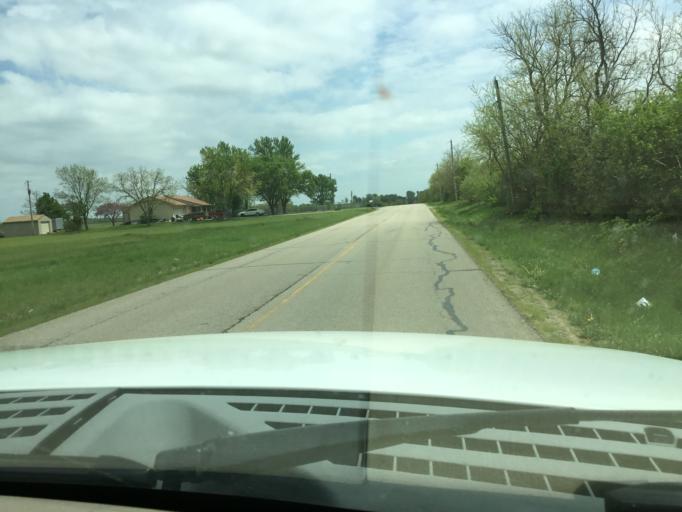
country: US
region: Kansas
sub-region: Shawnee County
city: Auburn
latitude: 38.9708
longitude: -95.8095
